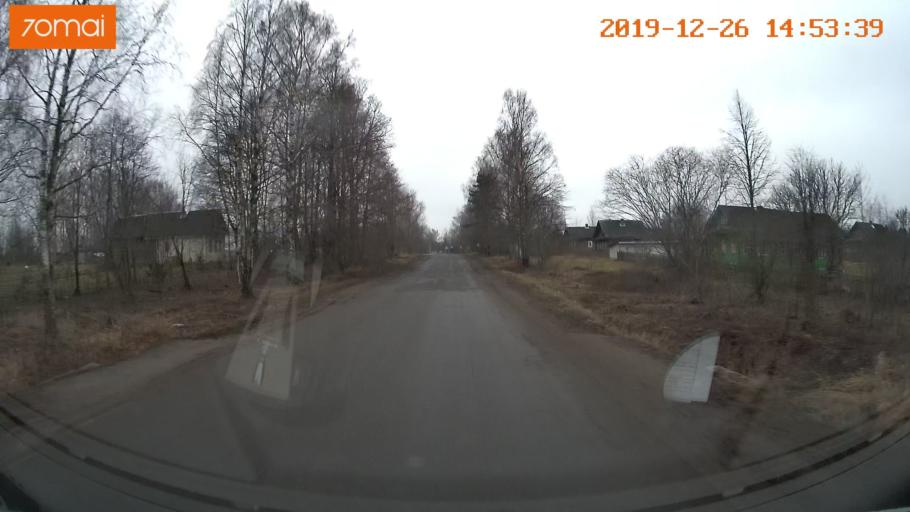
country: RU
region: Jaroslavl
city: Rybinsk
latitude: 58.3134
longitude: 38.8880
